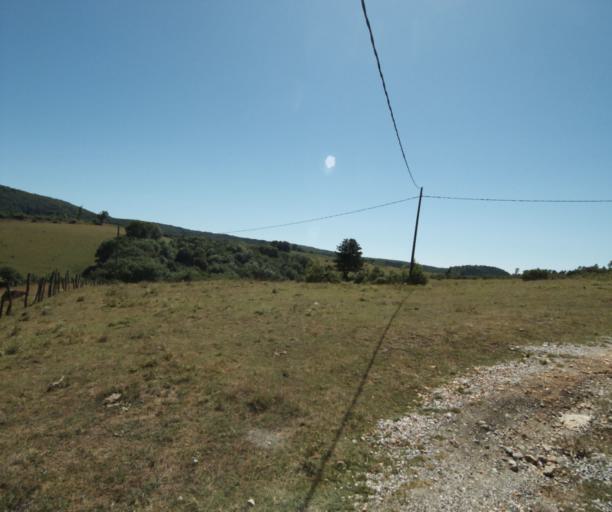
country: FR
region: Midi-Pyrenees
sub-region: Departement du Tarn
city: Soreze
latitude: 43.4471
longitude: 2.0942
